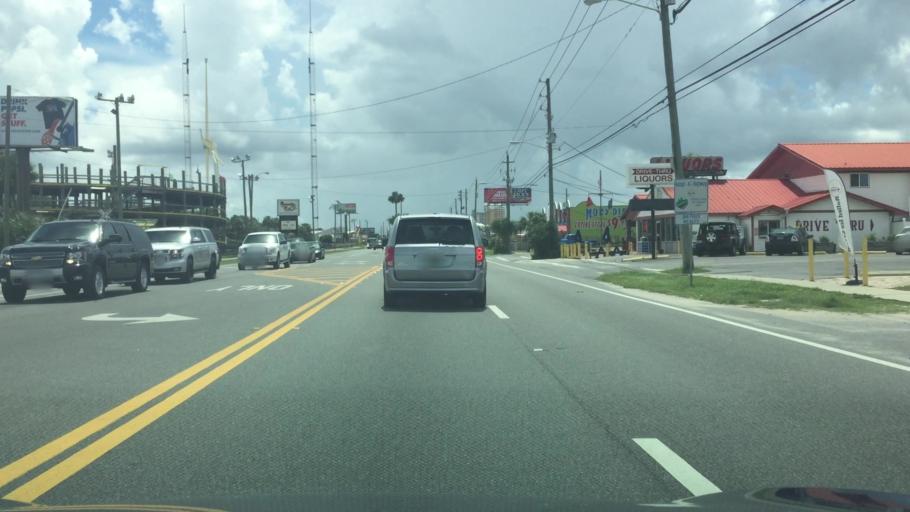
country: US
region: Florida
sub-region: Bay County
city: Panama City Beach
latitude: 30.1679
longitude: -85.7896
